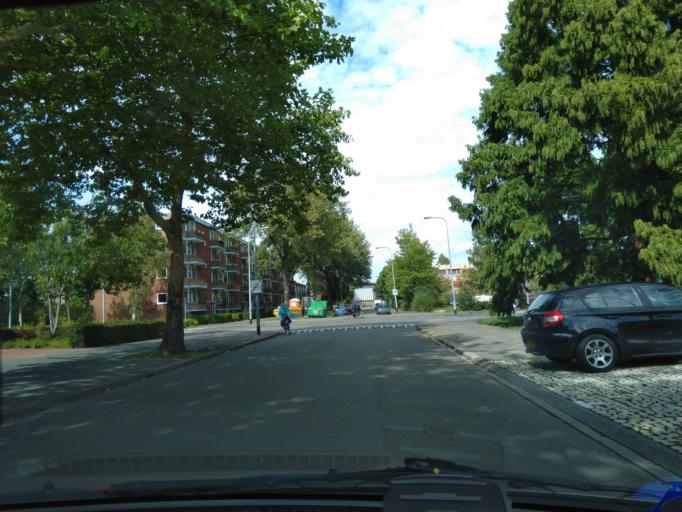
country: NL
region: Groningen
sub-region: Gemeente Groningen
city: Groningen
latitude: 53.1969
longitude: 6.5682
